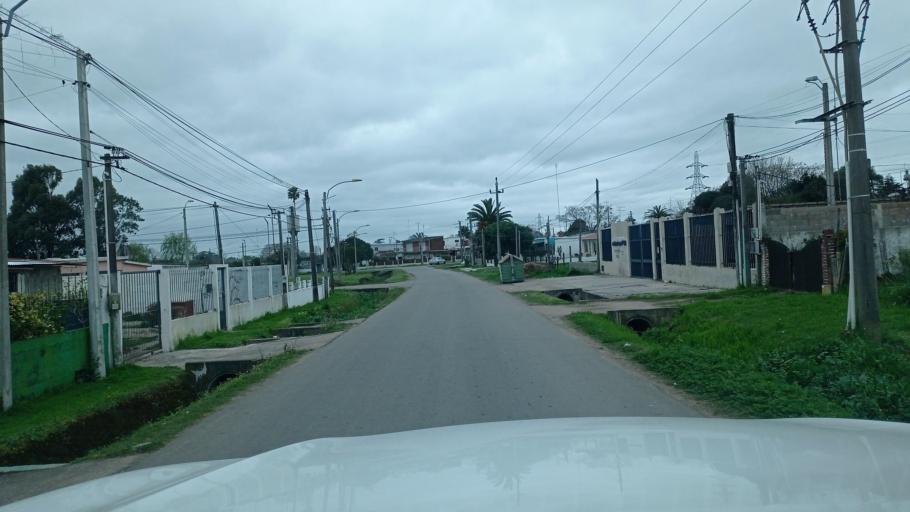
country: UY
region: Canelones
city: Toledo
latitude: -34.7783
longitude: -56.1362
